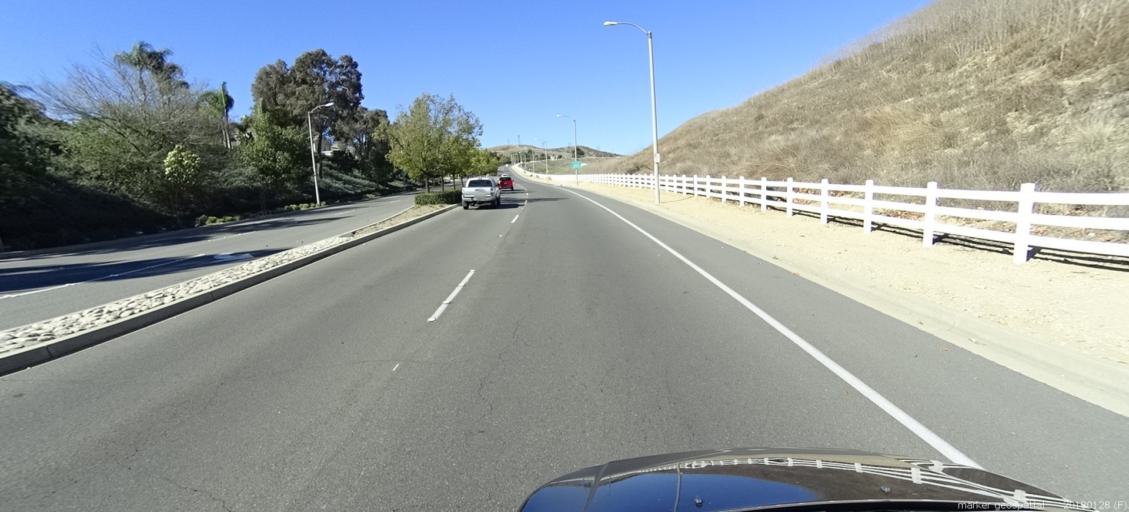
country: US
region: California
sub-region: San Bernardino County
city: Chino Hills
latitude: 33.9972
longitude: -117.7603
